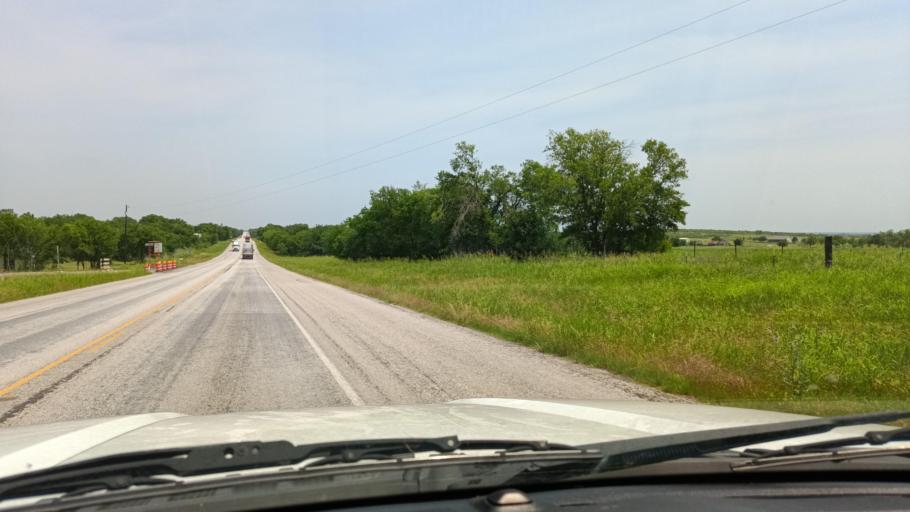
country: US
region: Texas
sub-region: Bell County
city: Rogers
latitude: 30.9466
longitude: -97.2472
